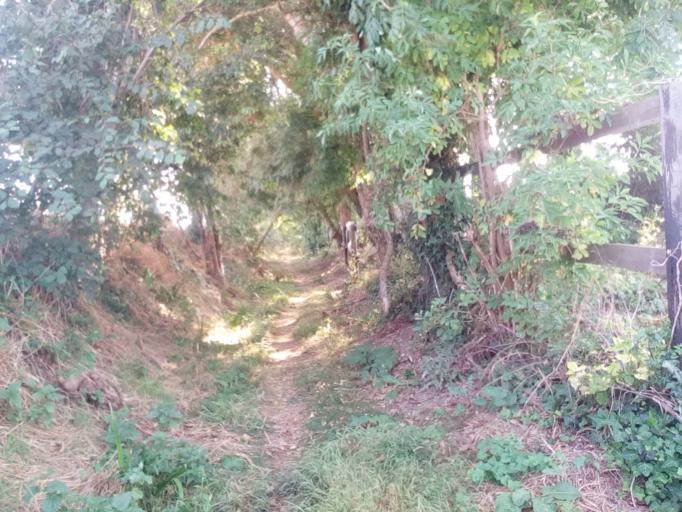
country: FR
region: Lower Normandy
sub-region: Departement du Calvados
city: Bernieres-sur-Mer
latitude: 49.3086
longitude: -0.4242
